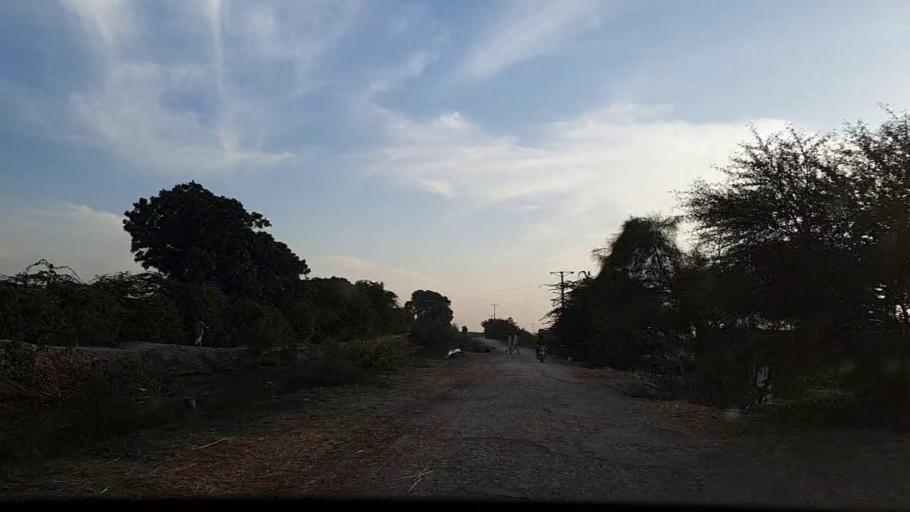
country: PK
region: Sindh
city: Mirpur Batoro
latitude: 24.6369
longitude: 68.1368
